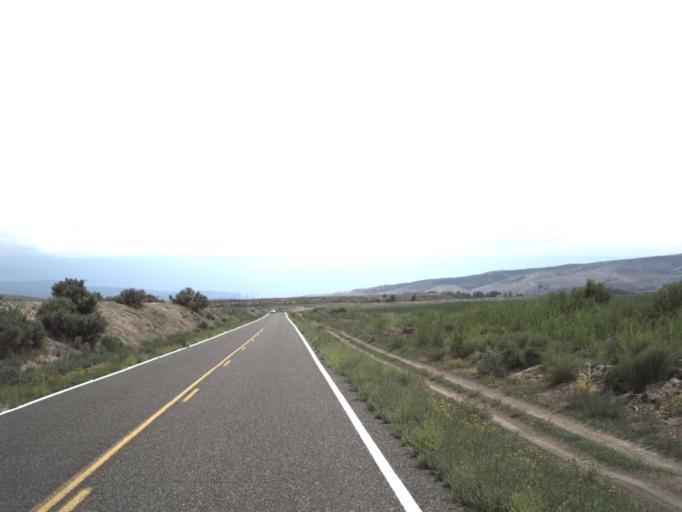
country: US
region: Utah
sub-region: Piute County
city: Junction
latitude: 38.1465
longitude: -111.9991
